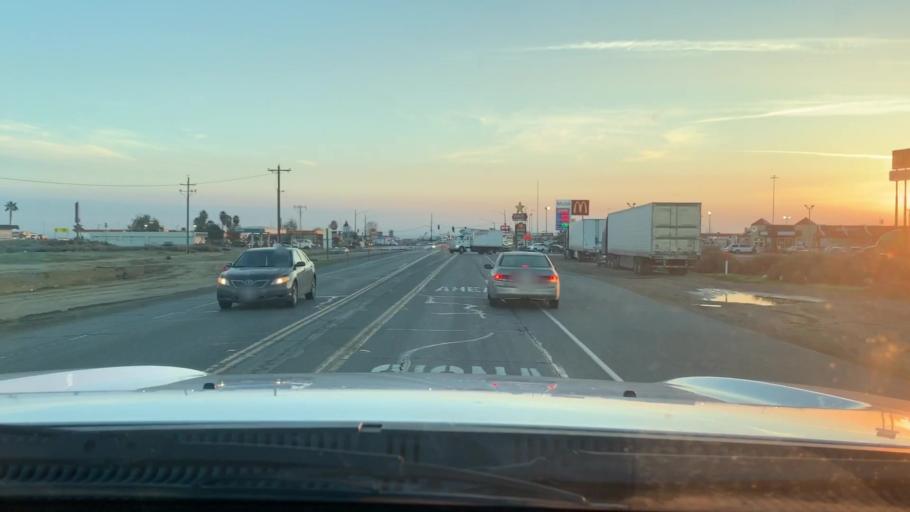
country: US
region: California
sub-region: Kern County
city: Lost Hills
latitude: 35.6161
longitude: -119.6623
